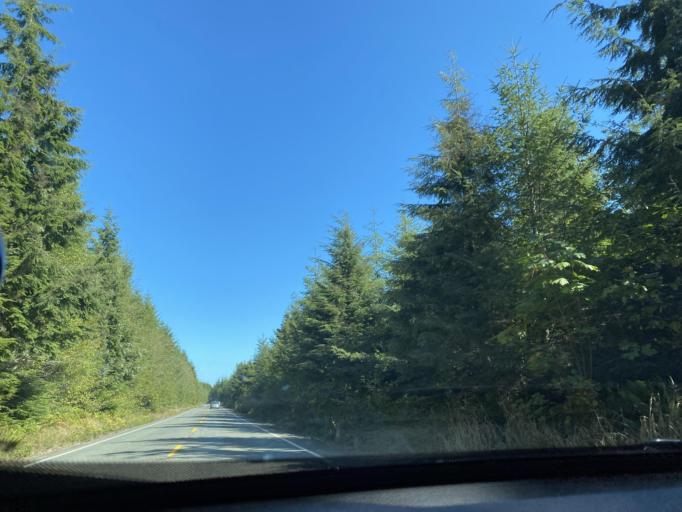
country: US
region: Washington
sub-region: Clallam County
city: Forks
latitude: 47.9312
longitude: -124.4812
